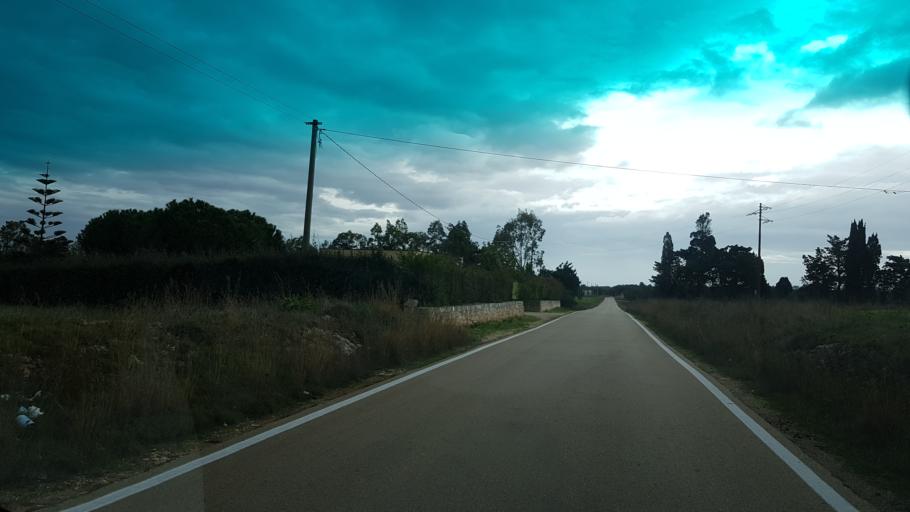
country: IT
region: Apulia
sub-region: Provincia di Brindisi
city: San Vito dei Normanni
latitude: 40.7134
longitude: 17.7654
